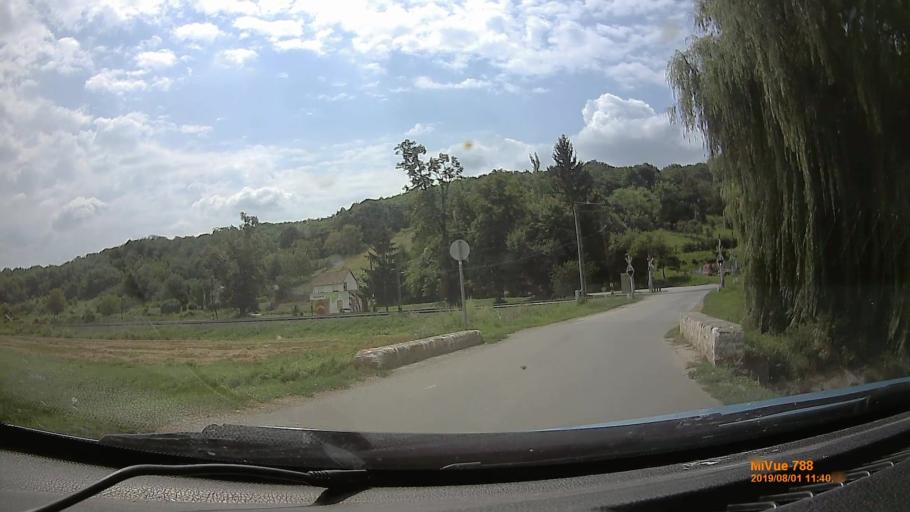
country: HU
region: Baranya
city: Villany
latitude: 45.8921
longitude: 18.3936
